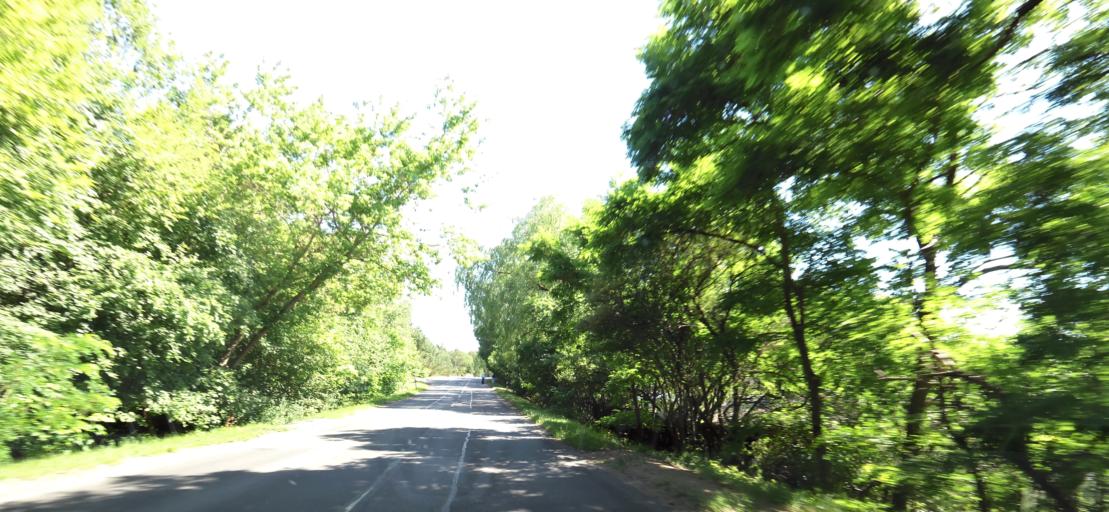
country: LT
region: Vilnius County
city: Rasos
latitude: 54.7930
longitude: 25.3508
